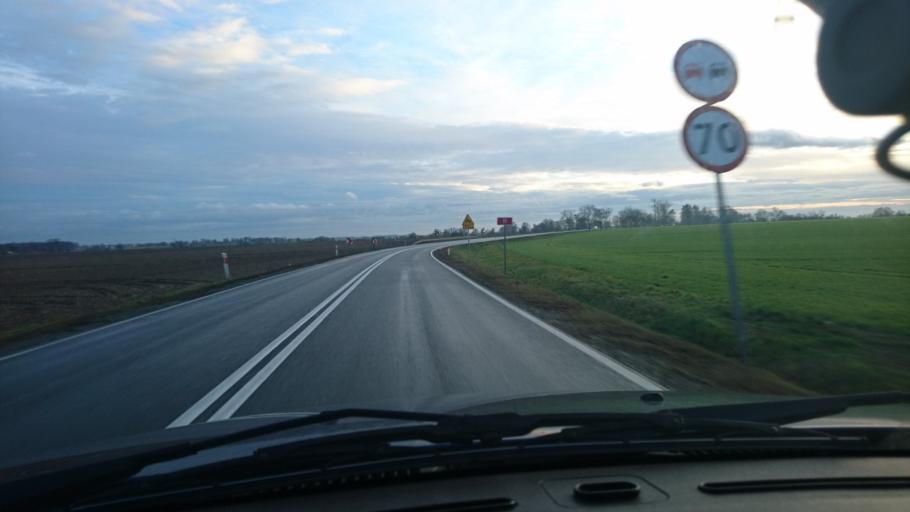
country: PL
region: Opole Voivodeship
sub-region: Powiat kluczborski
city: Byczyna
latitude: 51.0703
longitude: 18.2037
